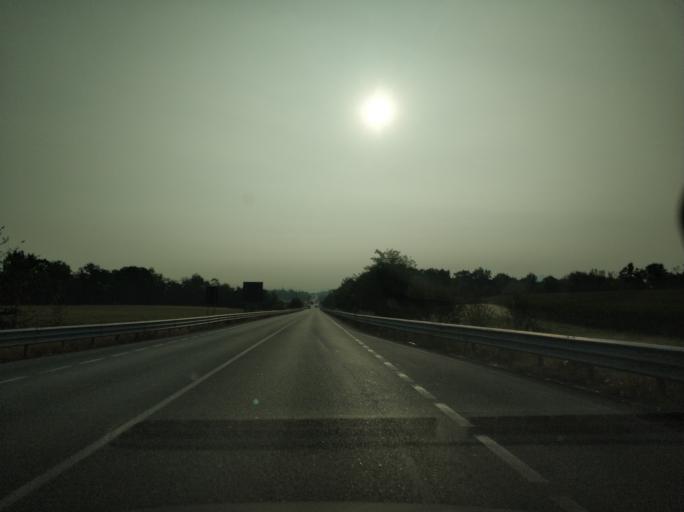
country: IT
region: Piedmont
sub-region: Provincia di Torino
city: Venaria Reale
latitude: 45.1511
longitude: 7.6251
